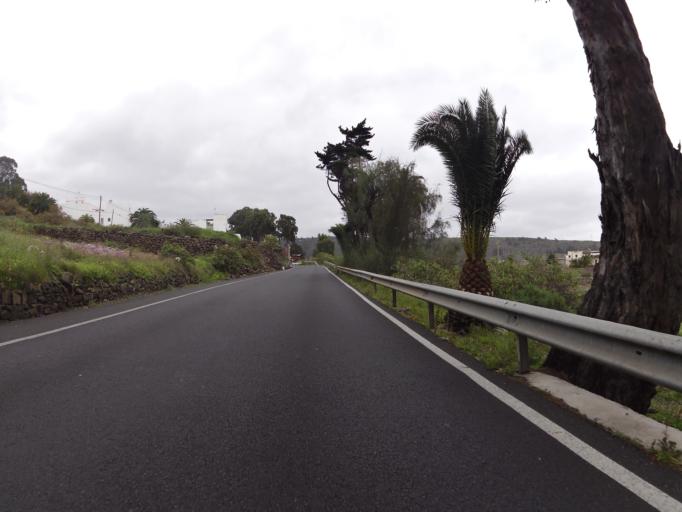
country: ES
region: Canary Islands
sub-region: Provincia de Las Palmas
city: Arucas
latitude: 28.0929
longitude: -15.5021
